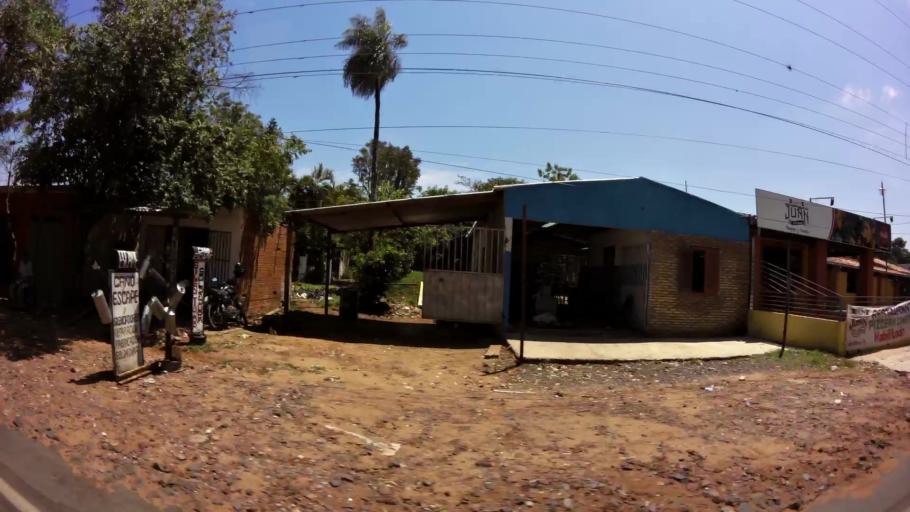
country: PY
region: Central
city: San Antonio
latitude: -25.4128
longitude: -57.5518
